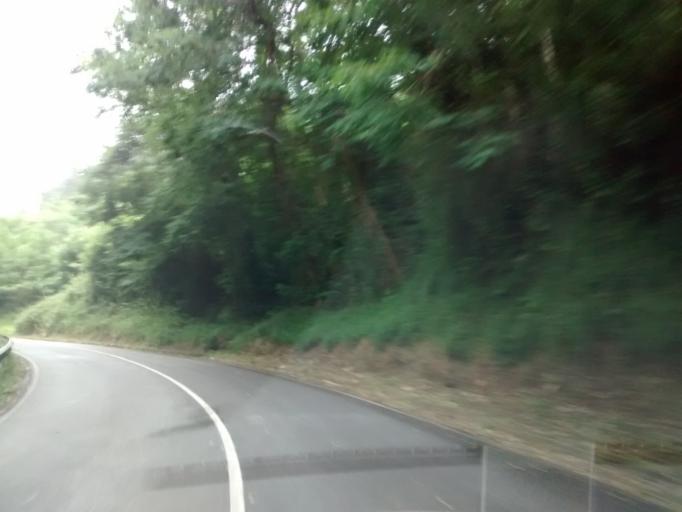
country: ES
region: Asturias
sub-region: Province of Asturias
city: Villaviciosa
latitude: 43.5441
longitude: -5.4068
